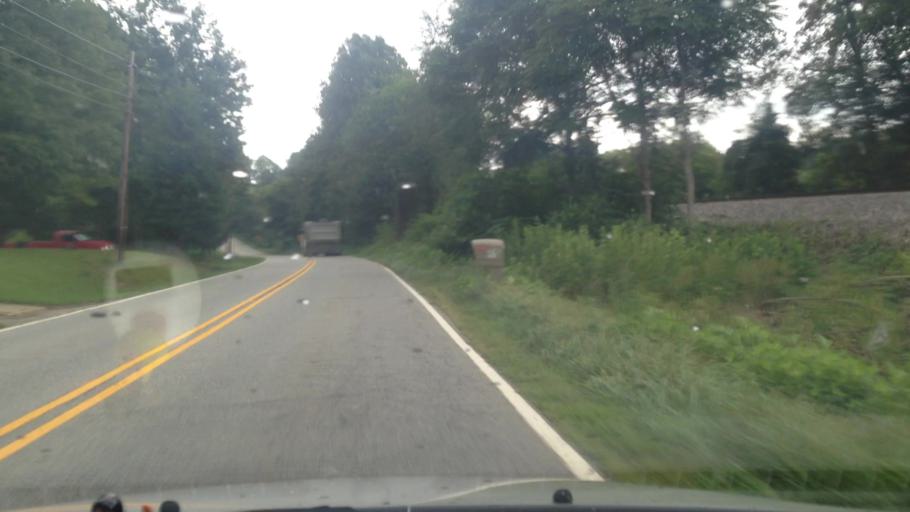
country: US
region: North Carolina
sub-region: Forsyth County
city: Walkertown
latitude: 36.1863
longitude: -80.1608
